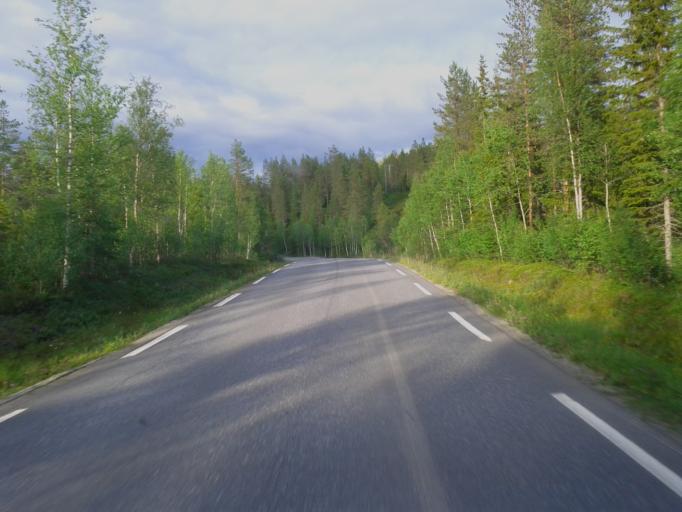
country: NO
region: Nordland
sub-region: Grane
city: Trofors
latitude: 65.5200
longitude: 13.6504
